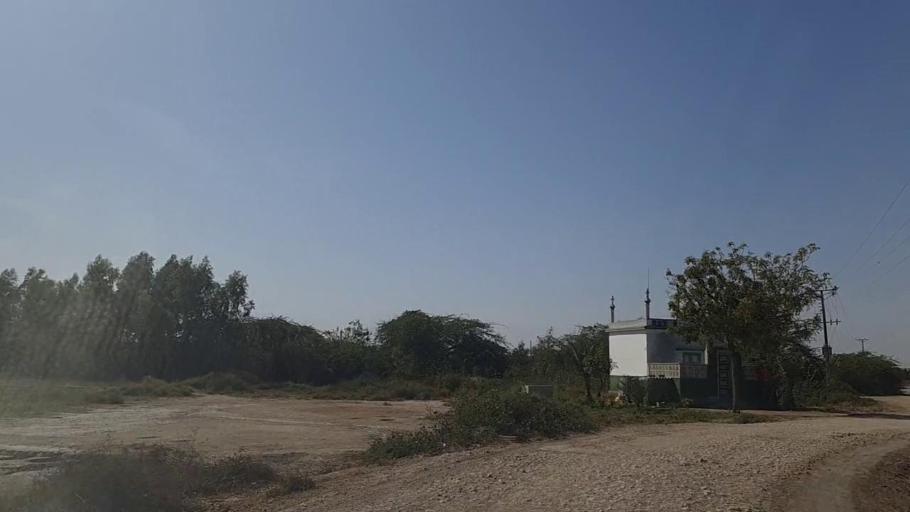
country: PK
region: Sindh
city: Thatta
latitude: 24.6385
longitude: 67.8843
